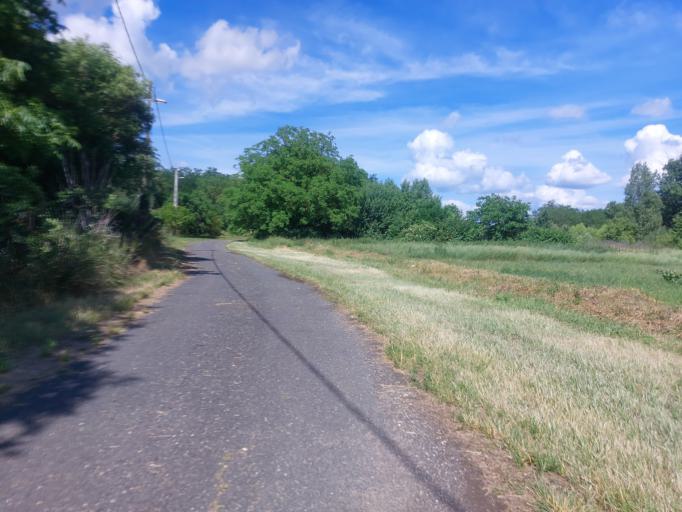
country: HU
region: Veszprem
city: Devecser
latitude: 47.1916
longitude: 17.3524
